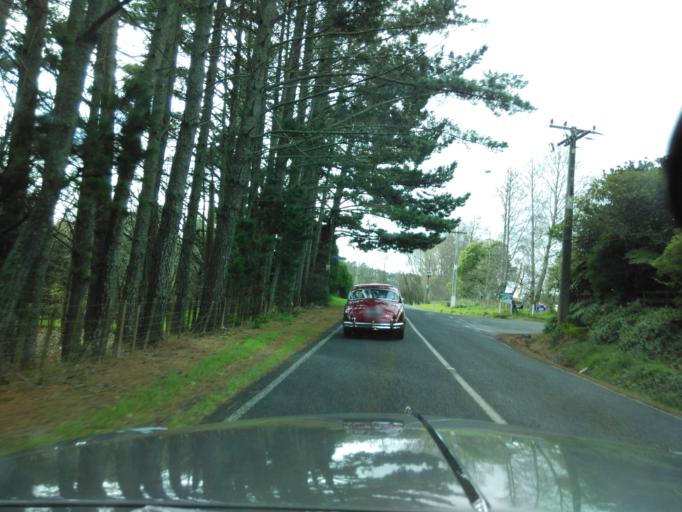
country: NZ
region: Auckland
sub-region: Auckland
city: Red Hill
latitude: -37.1372
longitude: 175.0419
